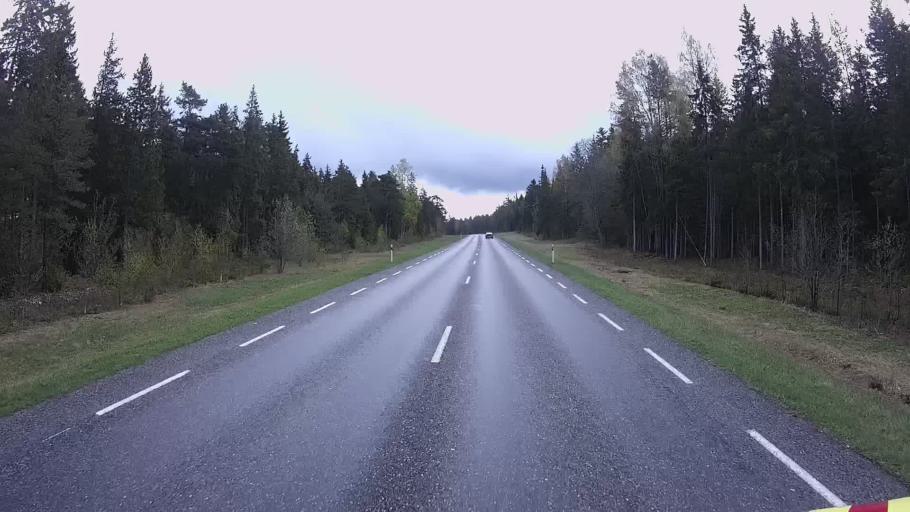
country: EE
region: Hiiumaa
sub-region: Kaerdla linn
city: Kardla
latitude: 58.9680
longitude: 22.8307
